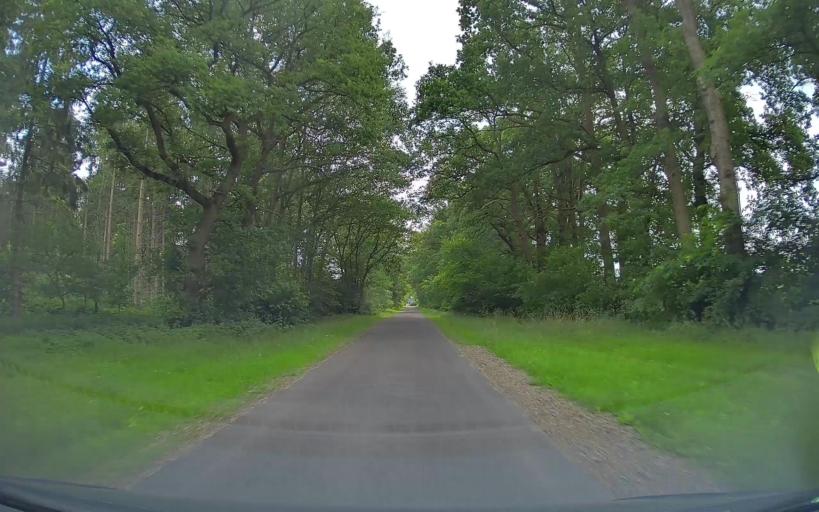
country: DE
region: Lower Saxony
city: Friesoythe
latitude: 52.9833
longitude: 7.8873
